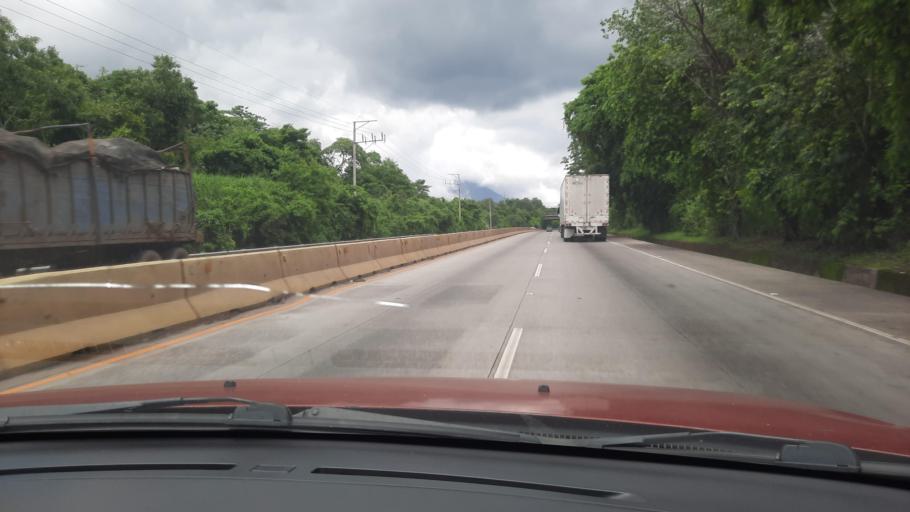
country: SV
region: Sonsonate
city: Sonzacate
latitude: 13.7372
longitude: -89.6978
